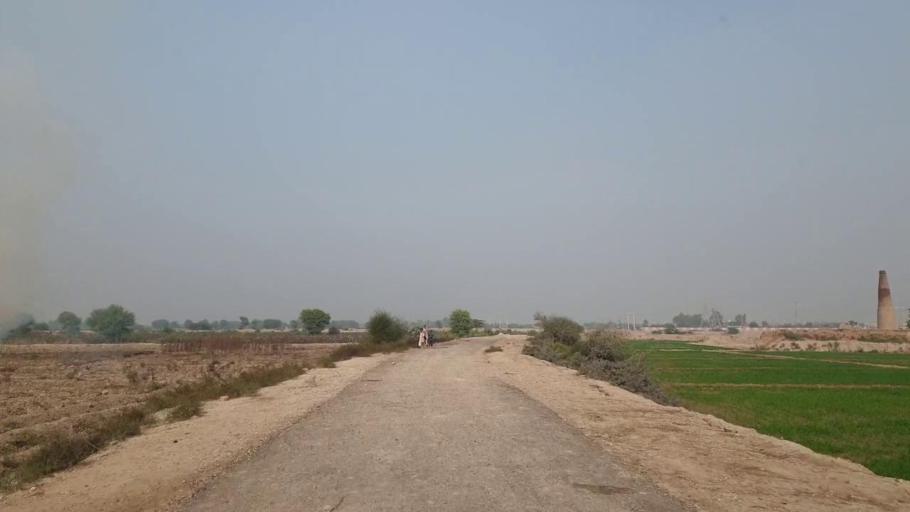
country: PK
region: Sindh
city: Bhan
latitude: 26.5433
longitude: 67.7091
